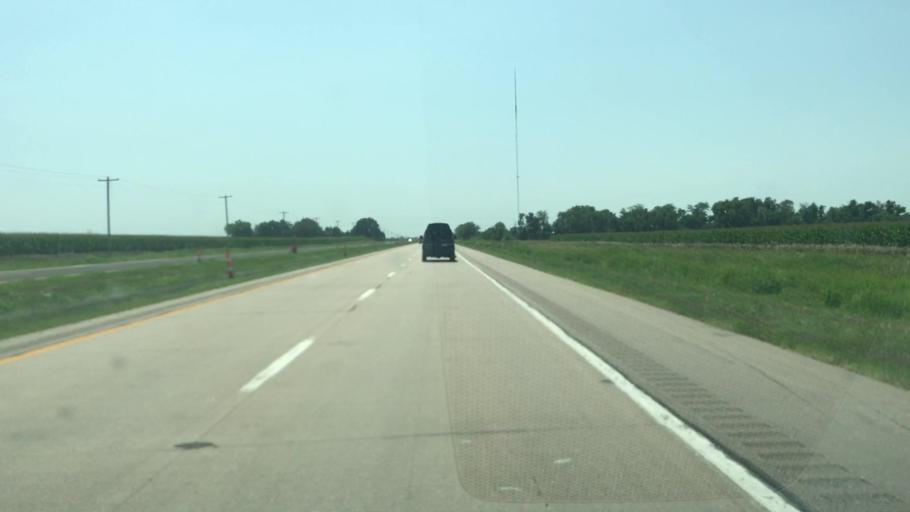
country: US
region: Nebraska
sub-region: Adams County
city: Hastings
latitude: 40.6600
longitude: -98.3824
